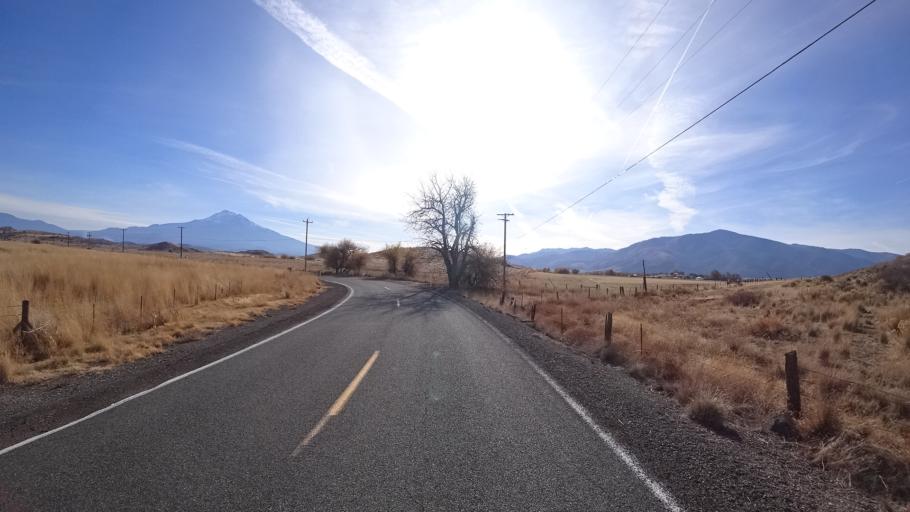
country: US
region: California
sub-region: Siskiyou County
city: Weed
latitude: 41.5355
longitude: -122.5182
